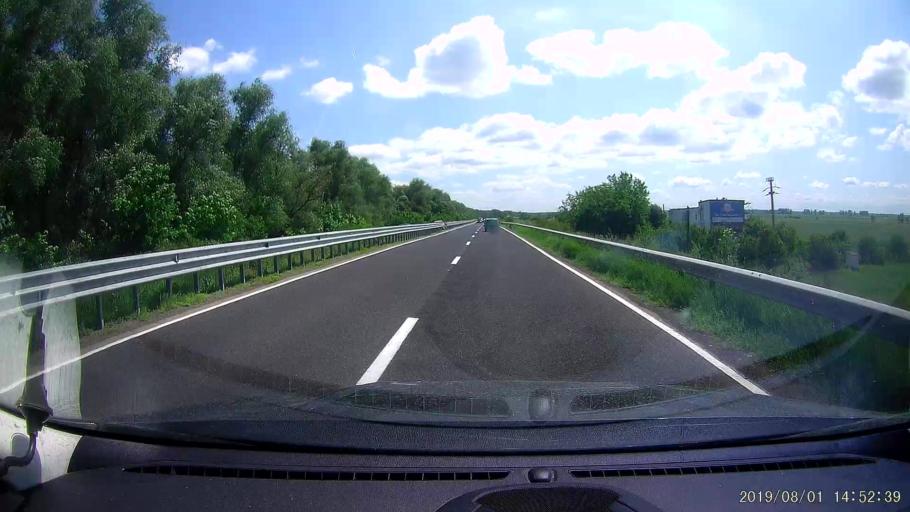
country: RO
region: Braila
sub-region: Comuna Vadeni
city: Vadeni
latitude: 45.3508
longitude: 28.0095
